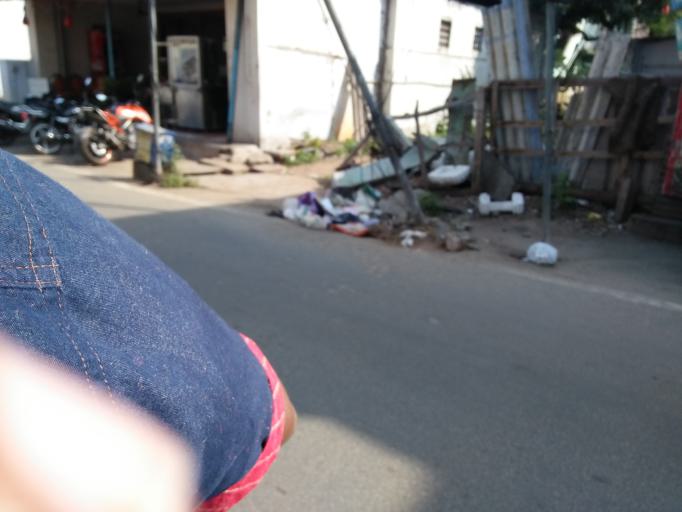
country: IN
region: Tamil Nadu
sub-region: Coimbatore
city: Coimbatore
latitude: 11.0223
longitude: 76.9631
